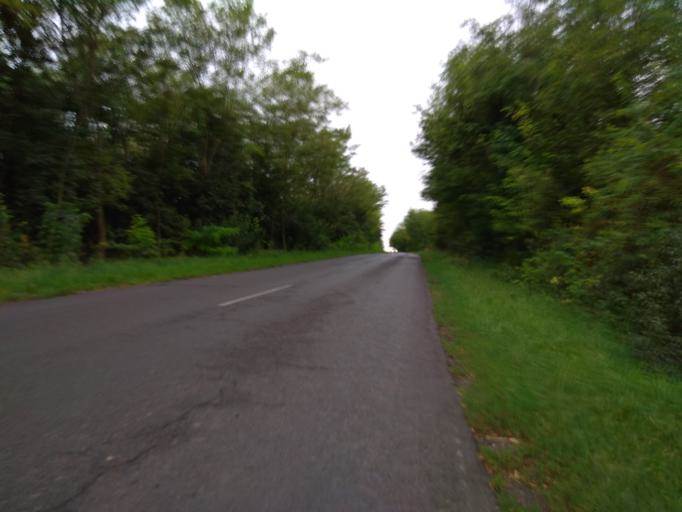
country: HU
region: Borsod-Abauj-Zemplen
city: Monok
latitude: 48.1738
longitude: 21.1146
